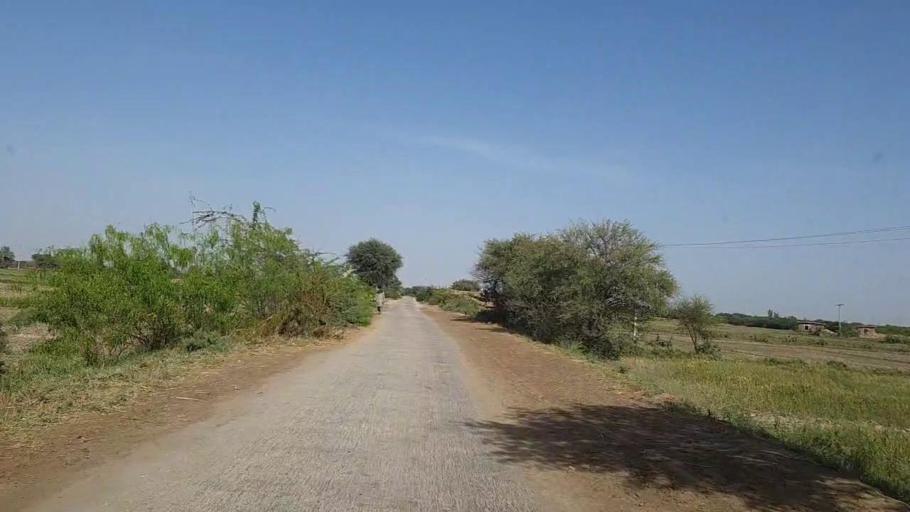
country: PK
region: Sindh
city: Kotri
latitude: 25.1682
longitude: 68.2864
